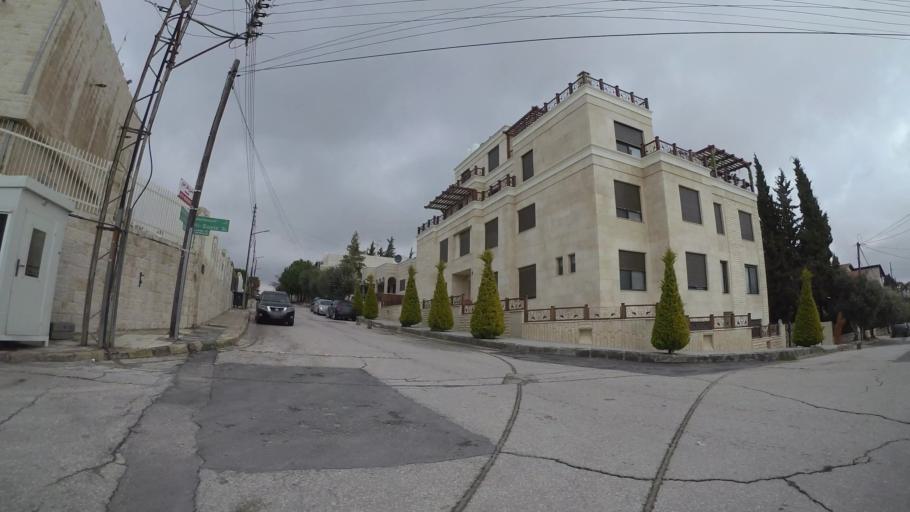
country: JO
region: Amman
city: Al Bunayyat ash Shamaliyah
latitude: 31.9500
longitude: 35.8811
